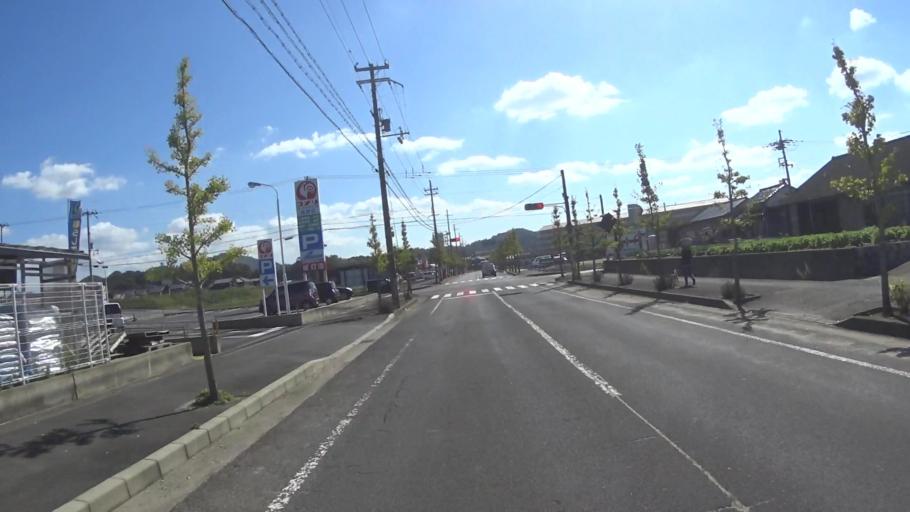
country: JP
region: Kyoto
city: Miyazu
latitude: 35.6798
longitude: 135.0229
